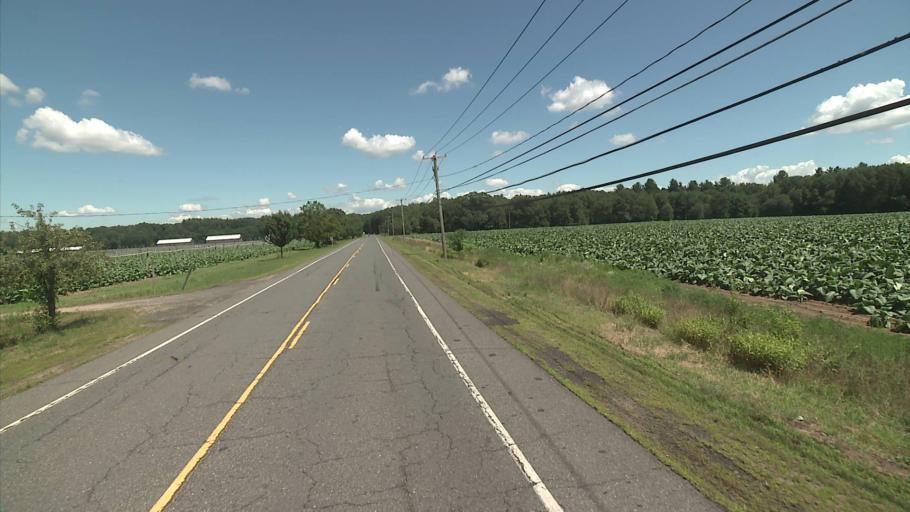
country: US
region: Massachusetts
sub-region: Hampden County
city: Southwick
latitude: 42.0189
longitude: -72.7453
